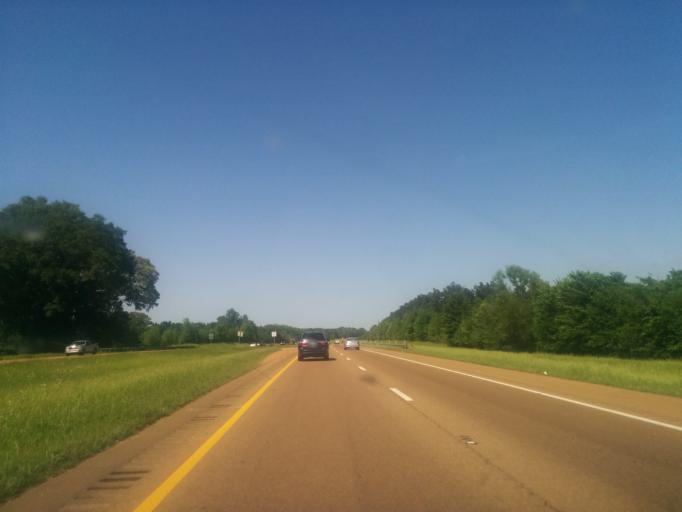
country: US
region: Mississippi
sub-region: Madison County
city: Madison
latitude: 32.4959
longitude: -90.1235
